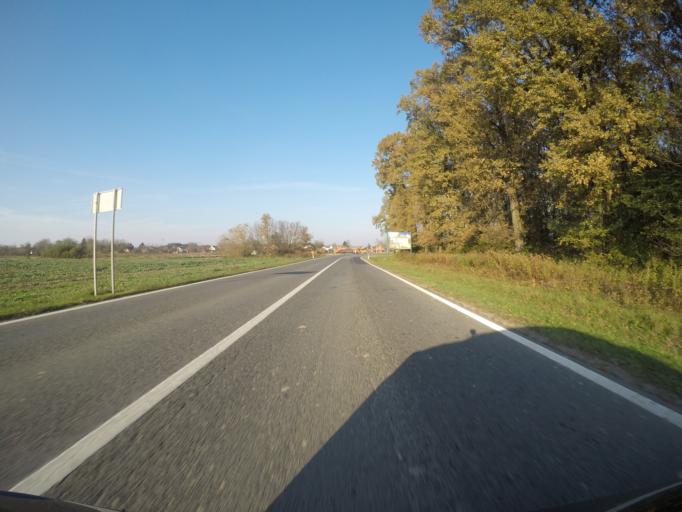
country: HR
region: Virovitick-Podravska
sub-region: Grad Virovitica
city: Virovitica
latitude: 45.8842
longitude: 17.4094
